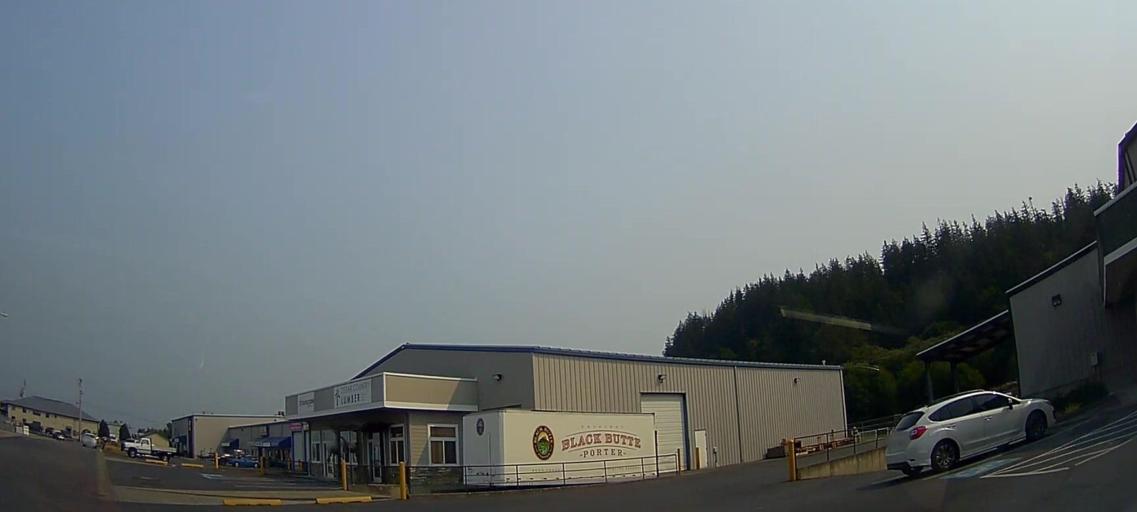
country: US
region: Washington
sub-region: Skagit County
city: Burlington
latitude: 48.4826
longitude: -122.3337
